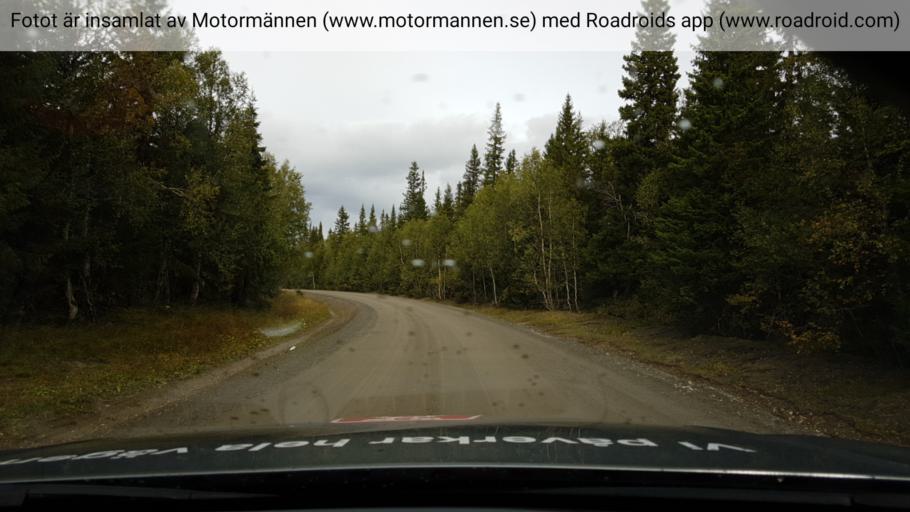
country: NO
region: Nord-Trondelag
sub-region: Snasa
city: Snaase
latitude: 63.7265
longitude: 12.4764
